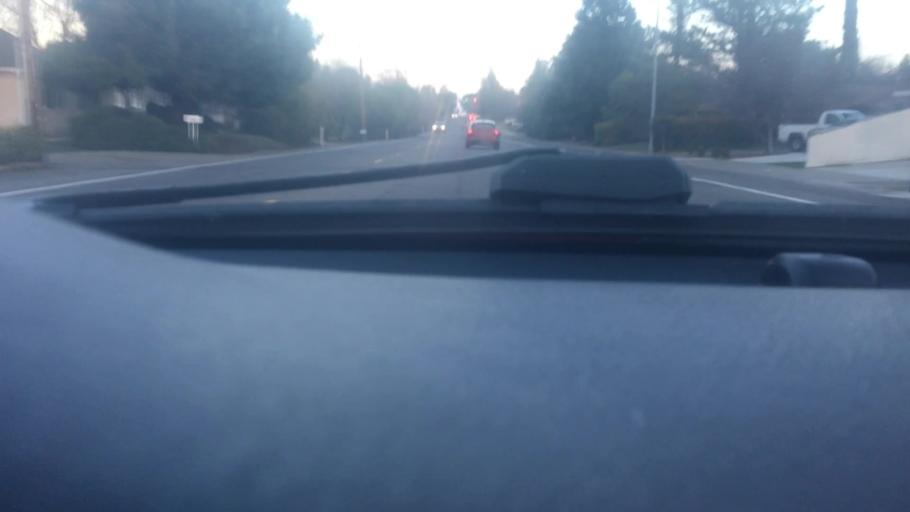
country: US
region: California
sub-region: Sacramento County
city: Carmichael
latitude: 38.6390
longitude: -121.3408
